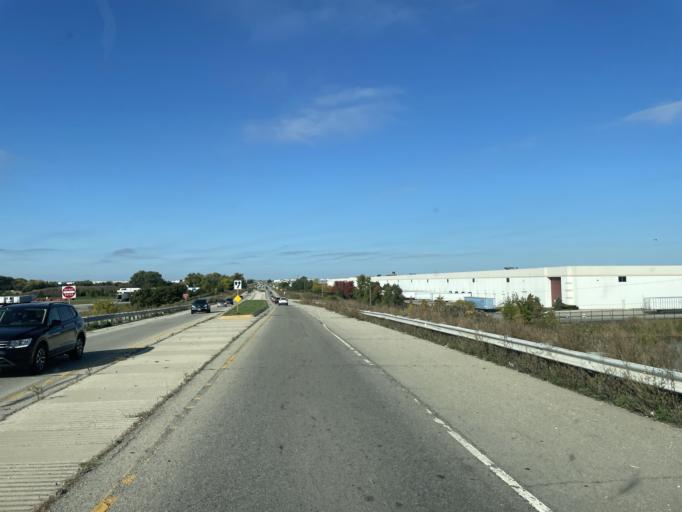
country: US
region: Wisconsin
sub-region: Kenosha County
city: Pleasant Prairie
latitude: 42.5890
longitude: -87.9062
